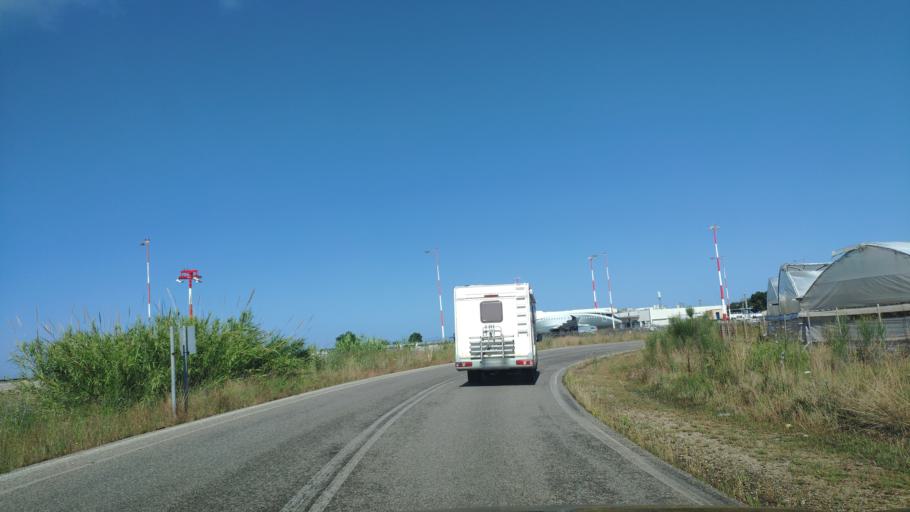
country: GR
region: Epirus
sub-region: Nomos Prevezis
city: Preveza
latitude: 38.9304
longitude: 20.7754
